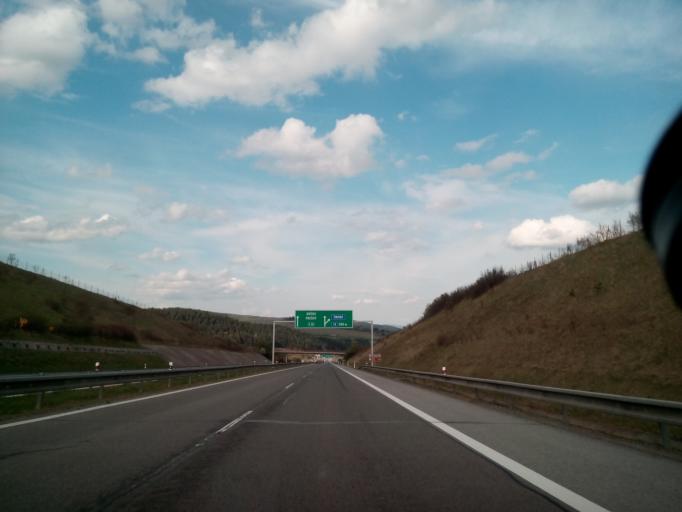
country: SK
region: Kosicky
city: Krompachy
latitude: 49.0028
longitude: 20.9324
